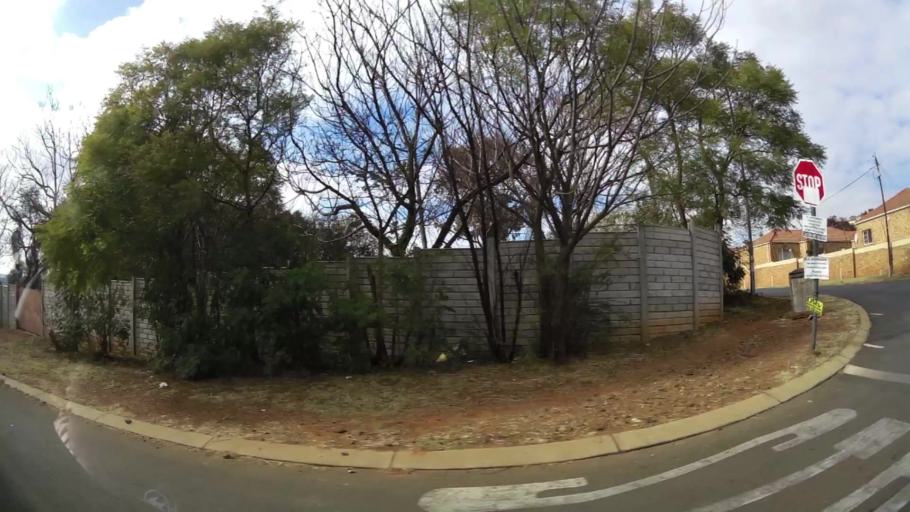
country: ZA
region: Gauteng
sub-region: City of Johannesburg Metropolitan Municipality
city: Roodepoort
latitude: -26.0978
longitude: 27.8711
